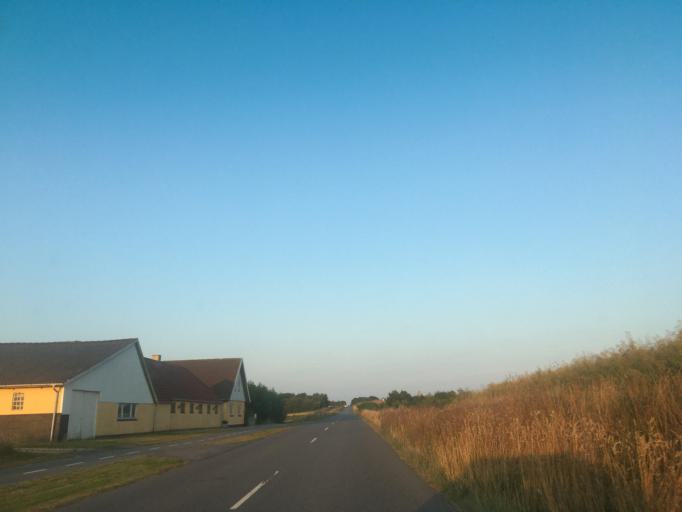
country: DK
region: North Denmark
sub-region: Thisted Kommune
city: Hurup
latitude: 56.7566
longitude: 8.3587
